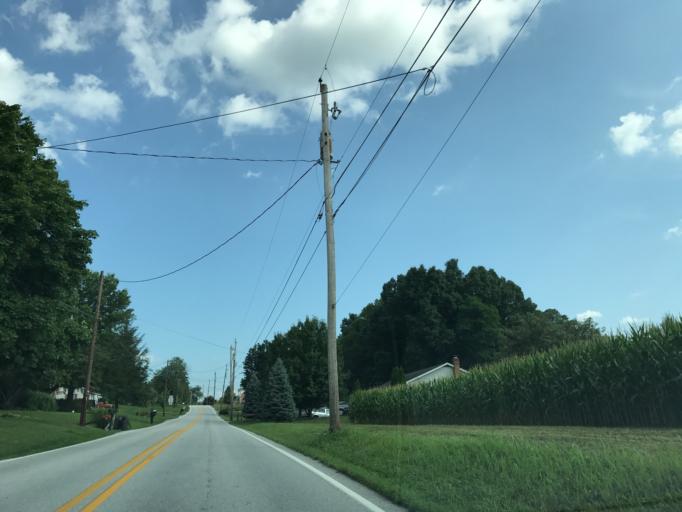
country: US
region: Pennsylvania
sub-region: Adams County
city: Mount Pleasant
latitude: 39.7556
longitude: -77.0356
